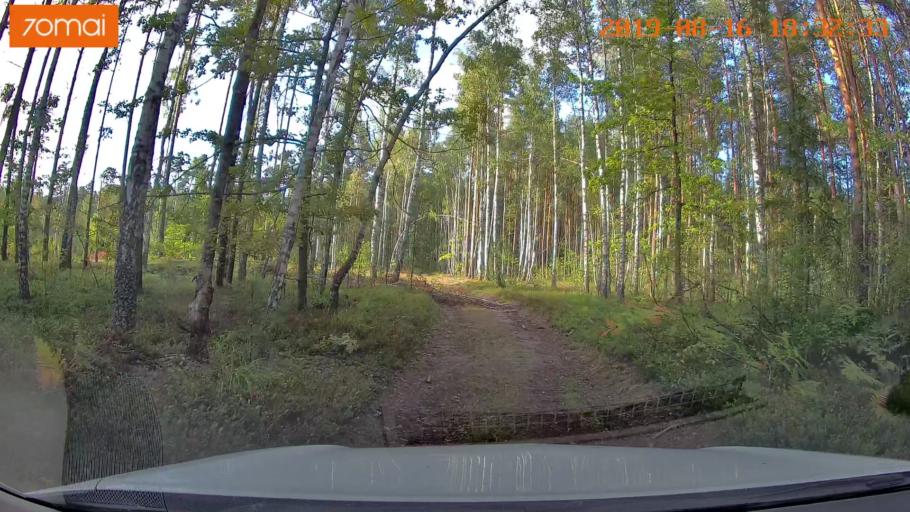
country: BY
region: Mogilev
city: Asipovichy
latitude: 53.1998
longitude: 28.6393
